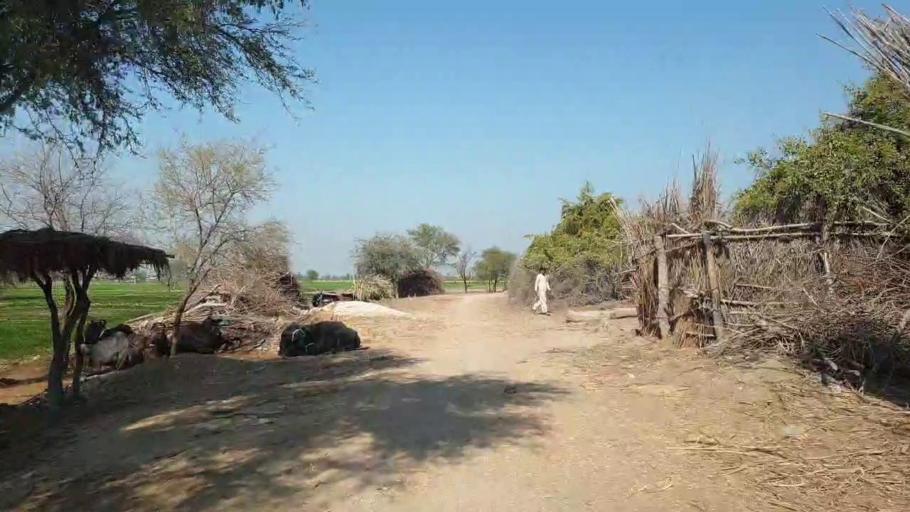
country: PK
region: Sindh
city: Shahdadpur
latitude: 25.9532
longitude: 68.5088
